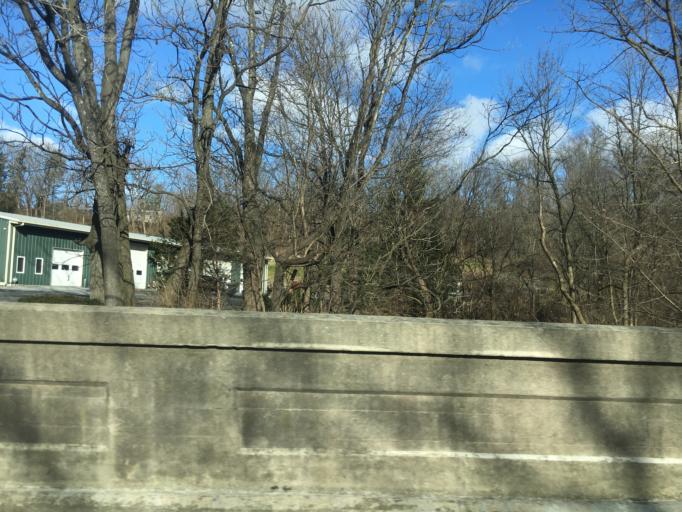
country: US
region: Pennsylvania
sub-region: Lehigh County
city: Egypt
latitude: 40.6782
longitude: -75.5275
